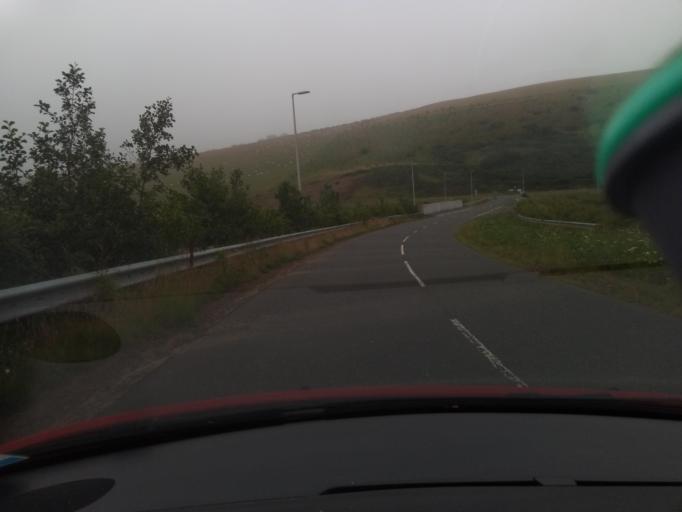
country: GB
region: Scotland
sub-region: Fife
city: Pathhead
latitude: 55.7766
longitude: -2.9517
